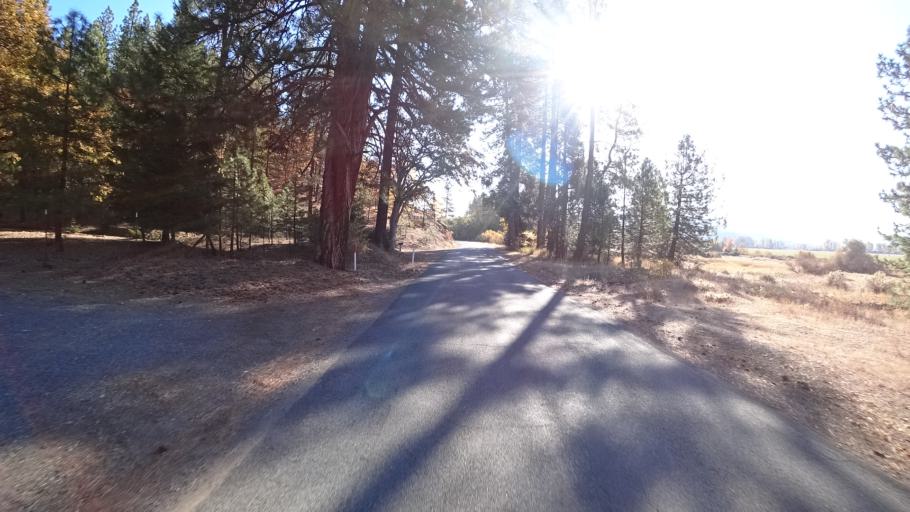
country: US
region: California
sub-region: Siskiyou County
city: Yreka
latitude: 41.6378
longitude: -122.9752
